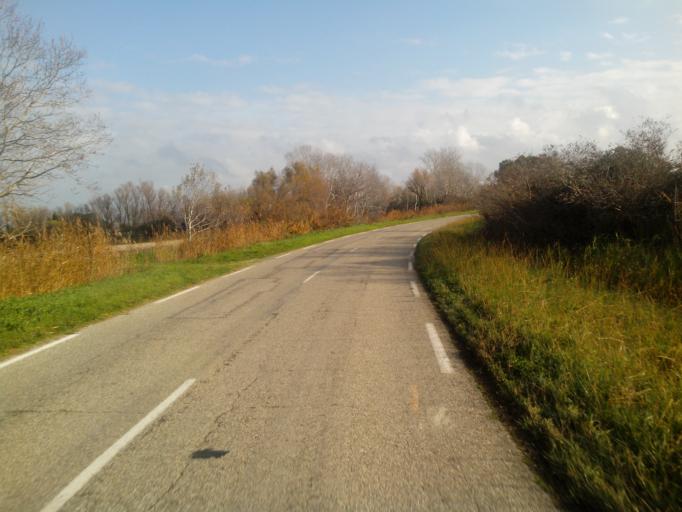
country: FR
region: Provence-Alpes-Cote d'Azur
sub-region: Departement des Bouches-du-Rhone
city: Arles
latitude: 43.5710
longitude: 4.5578
